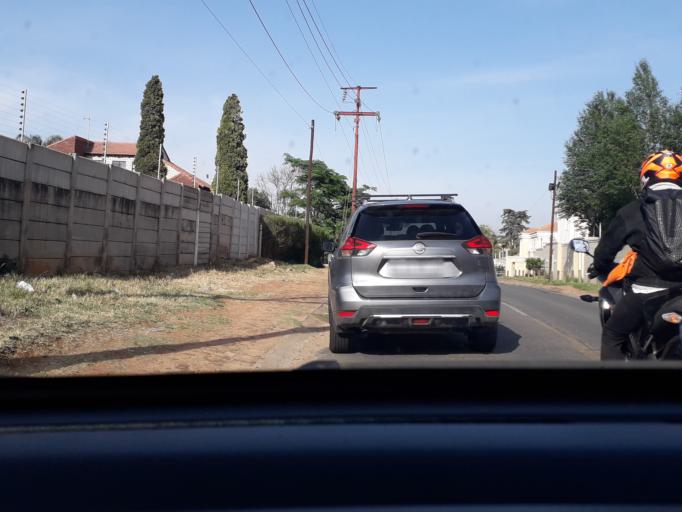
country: ZA
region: Gauteng
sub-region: City of Johannesburg Metropolitan Municipality
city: Midrand
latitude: -26.0665
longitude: 28.0579
